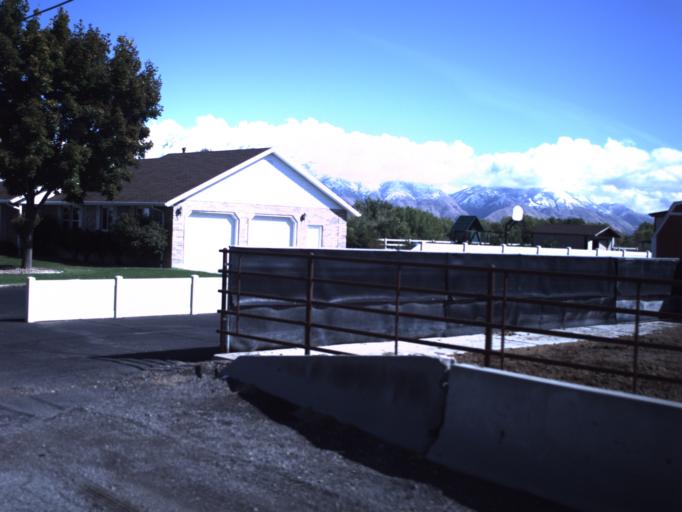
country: US
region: Utah
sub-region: Utah County
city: Spanish Fork
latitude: 40.0988
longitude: -111.6808
